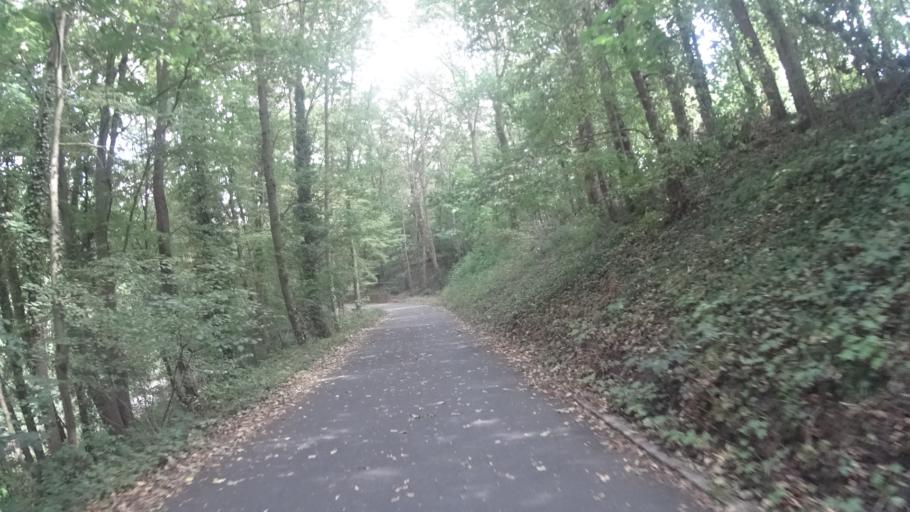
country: FR
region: Ile-de-France
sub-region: Departement de Seine-Saint-Denis
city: Tremblay-en-France
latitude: 48.9460
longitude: 2.5786
